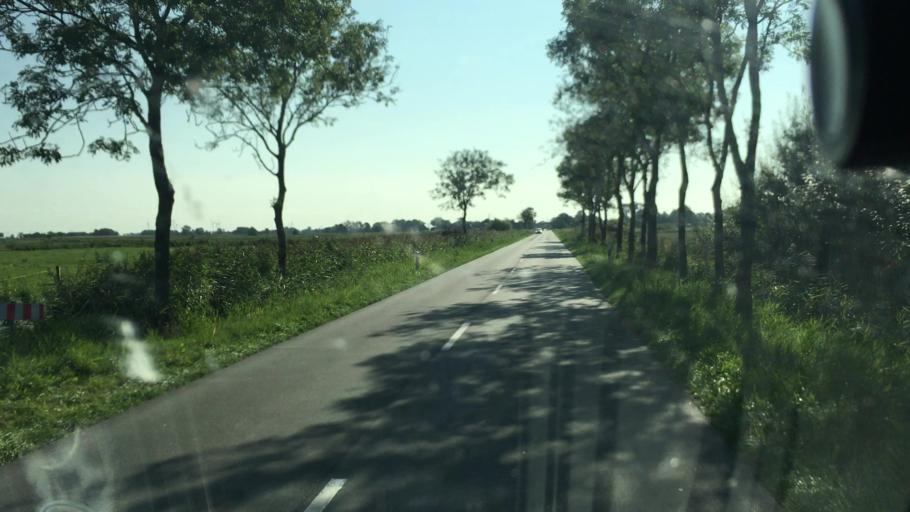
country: DE
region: Lower Saxony
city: Werdum
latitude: 53.6628
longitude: 7.7011
